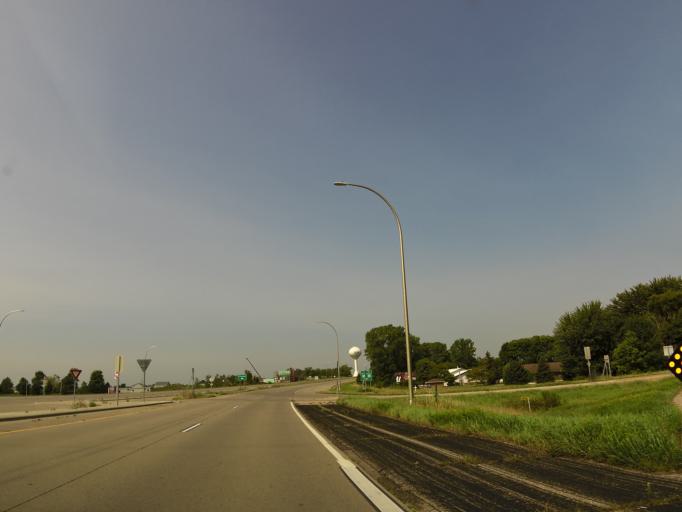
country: US
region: Minnesota
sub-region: Carver County
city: Cologne
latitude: 44.7653
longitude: -93.7806
